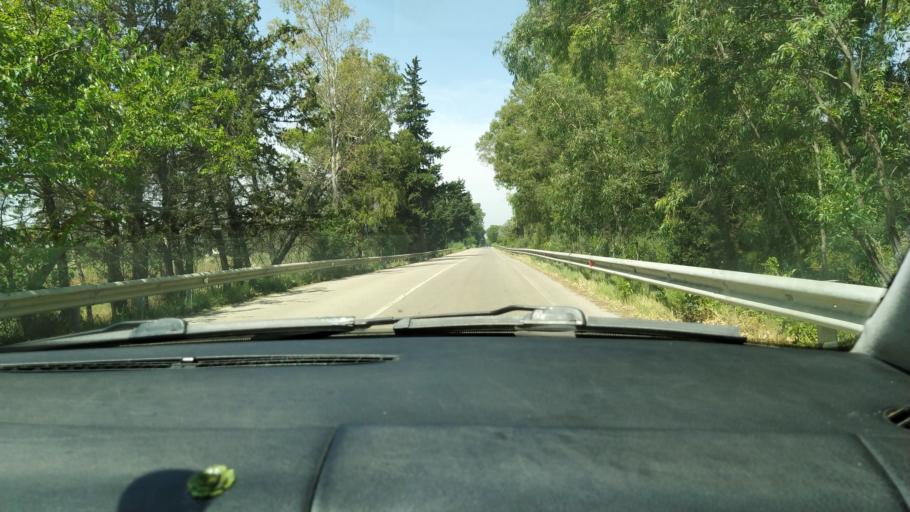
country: IT
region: Apulia
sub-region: Provincia di Taranto
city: Marina di Ginosa
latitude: 40.3720
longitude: 16.8069
